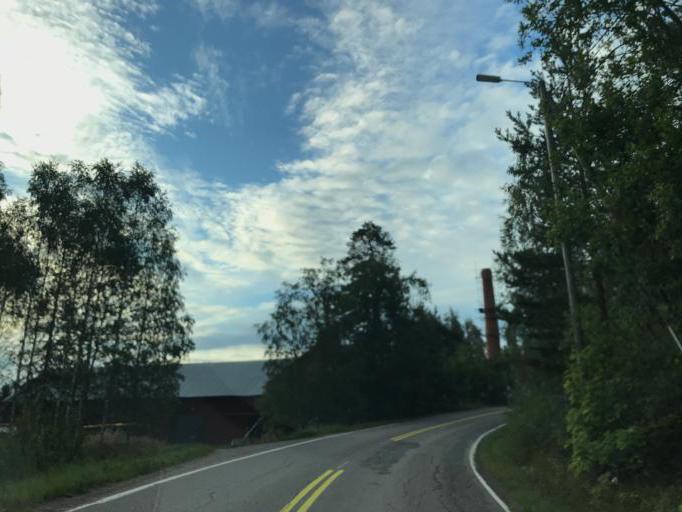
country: FI
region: Uusimaa
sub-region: Helsinki
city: Vihti
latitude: 60.3866
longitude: 24.5220
